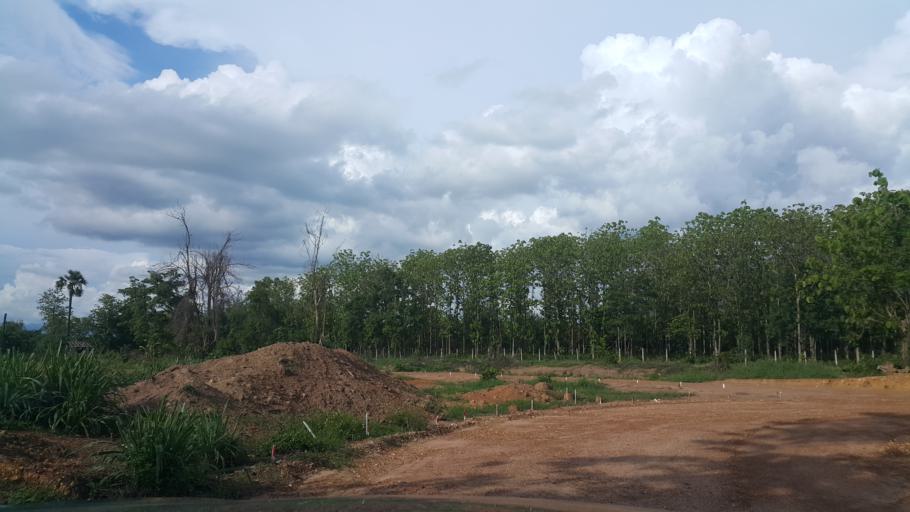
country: TH
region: Chiang Mai
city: Mae On
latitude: 18.7232
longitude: 99.2159
